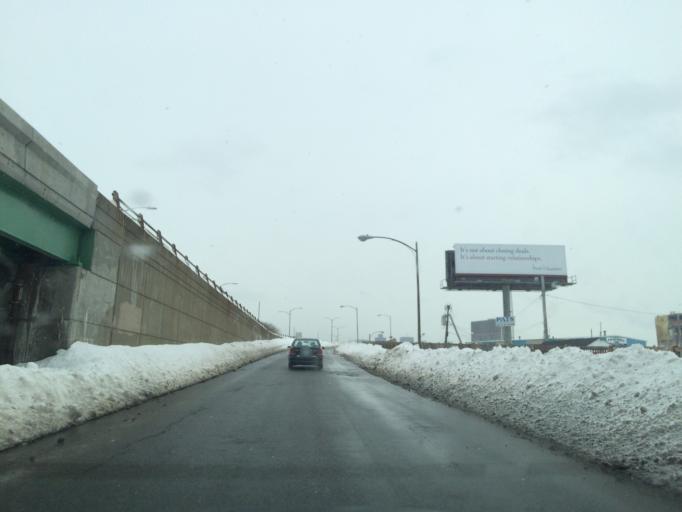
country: US
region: Massachusetts
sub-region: Middlesex County
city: Somerville
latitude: 42.3767
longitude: -71.0881
